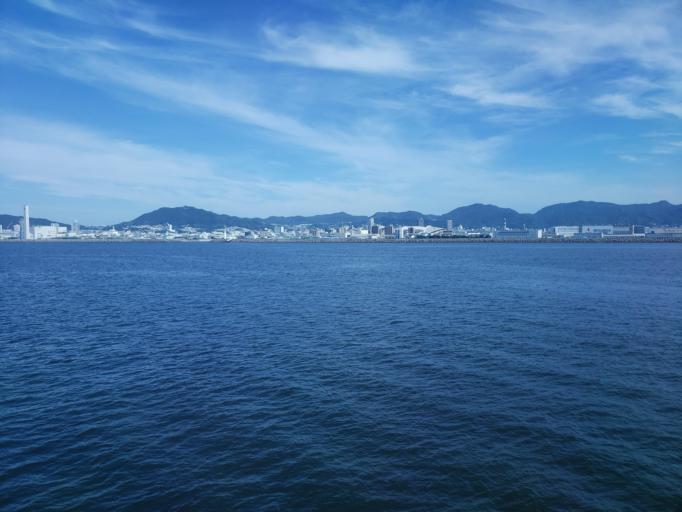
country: JP
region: Hyogo
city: Kobe
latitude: 34.6400
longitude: 135.1773
